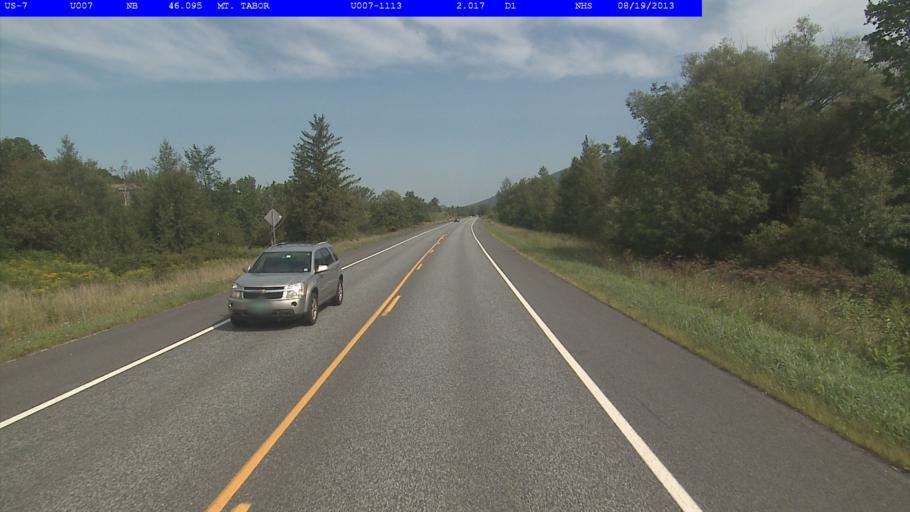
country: US
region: Vermont
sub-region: Bennington County
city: Manchester Center
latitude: 43.3341
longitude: -72.9923
